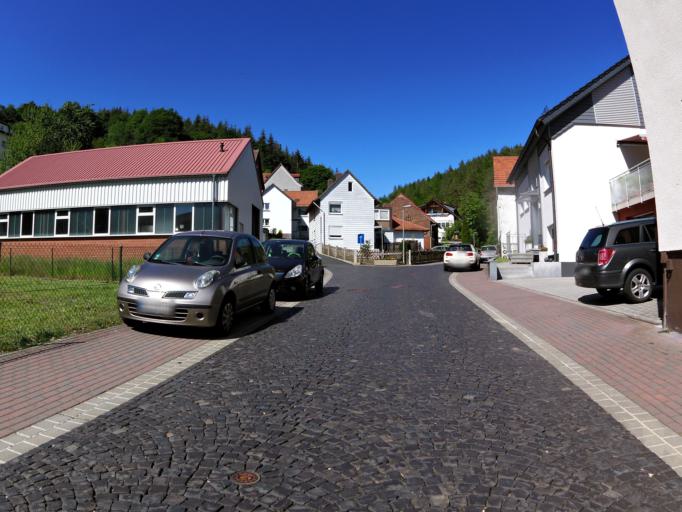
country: DE
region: Hesse
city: Philippsthal
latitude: 50.8444
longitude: 10.0078
